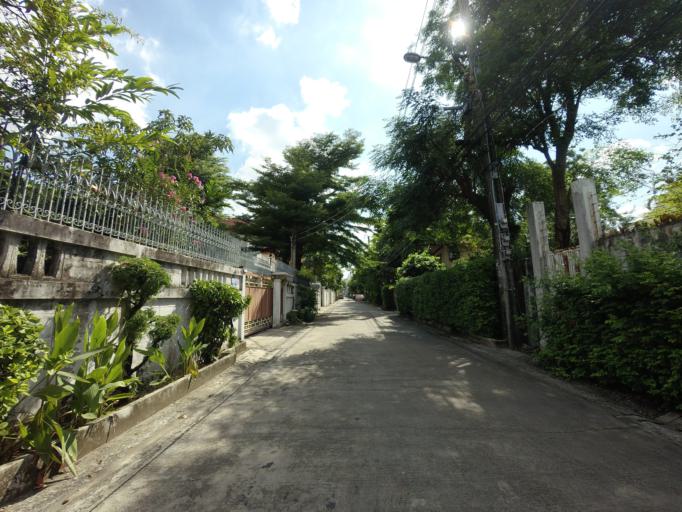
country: TH
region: Bangkok
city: Huai Khwang
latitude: 13.7871
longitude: 100.5934
